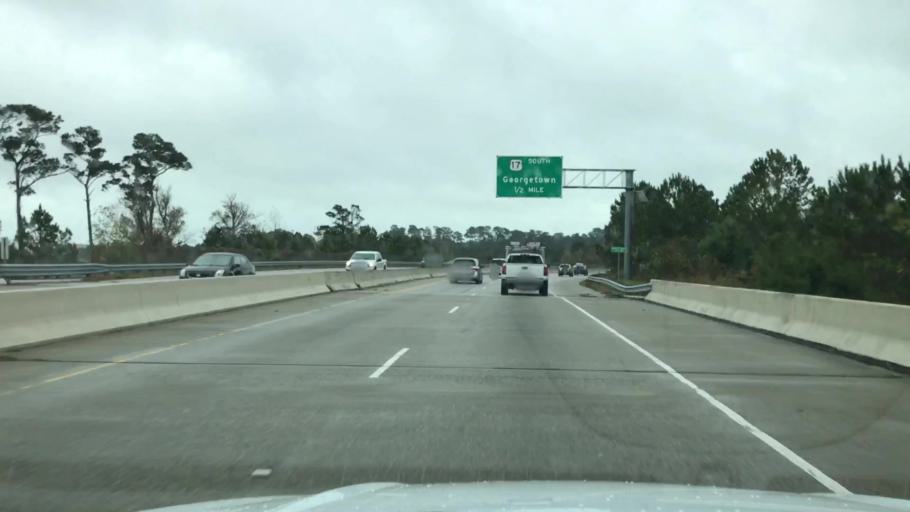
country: US
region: South Carolina
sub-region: Horry County
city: Myrtle Beach
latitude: 33.7492
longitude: -78.8487
